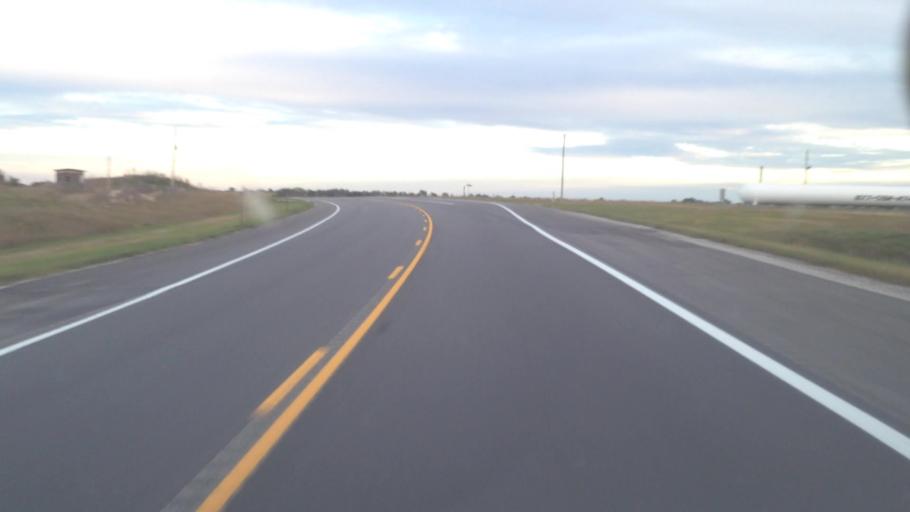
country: US
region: Kansas
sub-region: Franklin County
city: Ottawa
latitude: 38.4722
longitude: -95.2660
